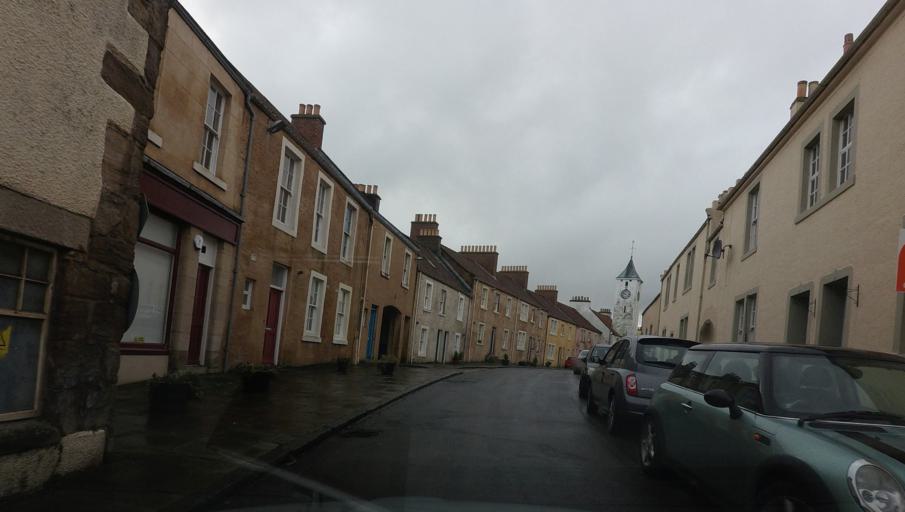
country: GB
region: Scotland
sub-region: Fife
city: East Wemyss
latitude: 56.1403
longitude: -3.0851
